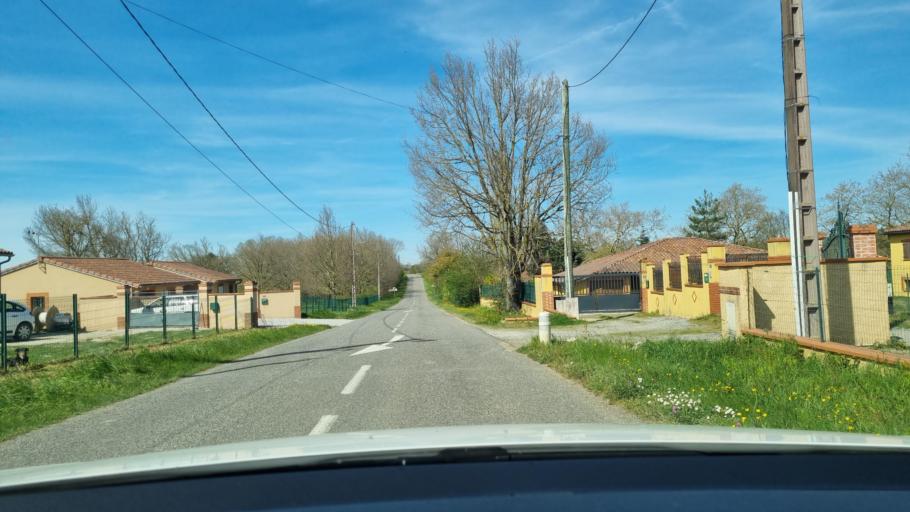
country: FR
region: Midi-Pyrenees
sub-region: Departement de la Haute-Garonne
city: Rieumes
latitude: 43.4695
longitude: 1.0629
